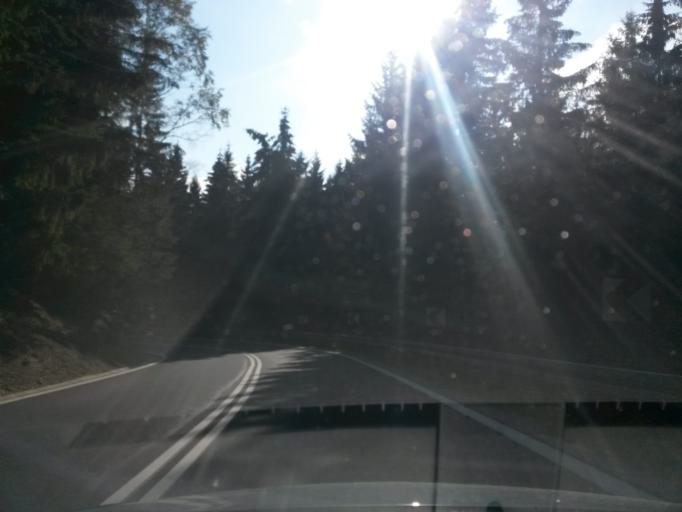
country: PL
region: Lower Silesian Voivodeship
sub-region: Powiat jeleniogorski
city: Szklarska Poreba
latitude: 50.8256
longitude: 15.4842
